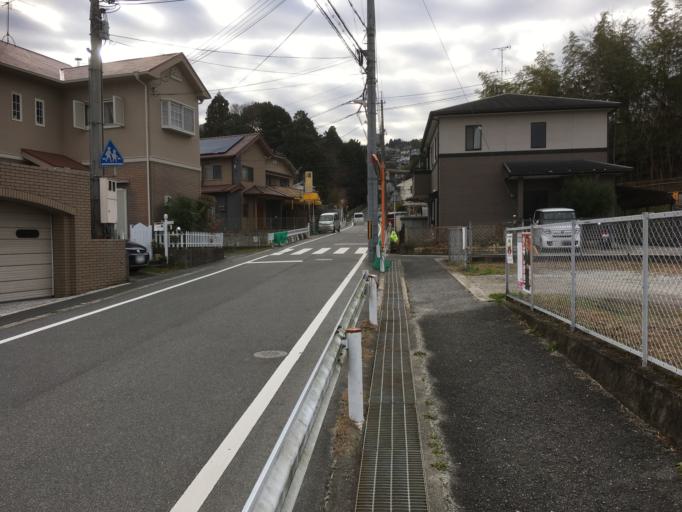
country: JP
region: Nara
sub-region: Ikoma-shi
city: Ikoma
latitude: 34.7003
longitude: 135.6950
